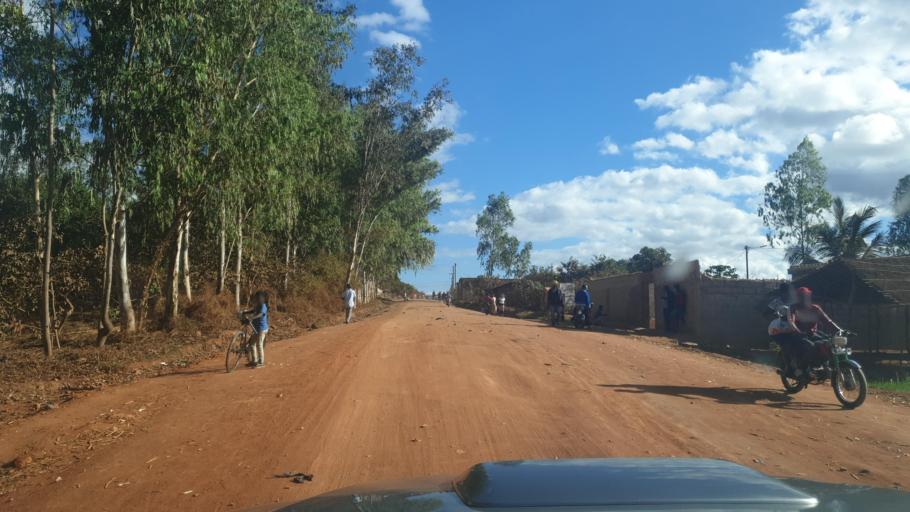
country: MZ
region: Nampula
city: Nampula
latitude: -15.0978
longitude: 39.2243
